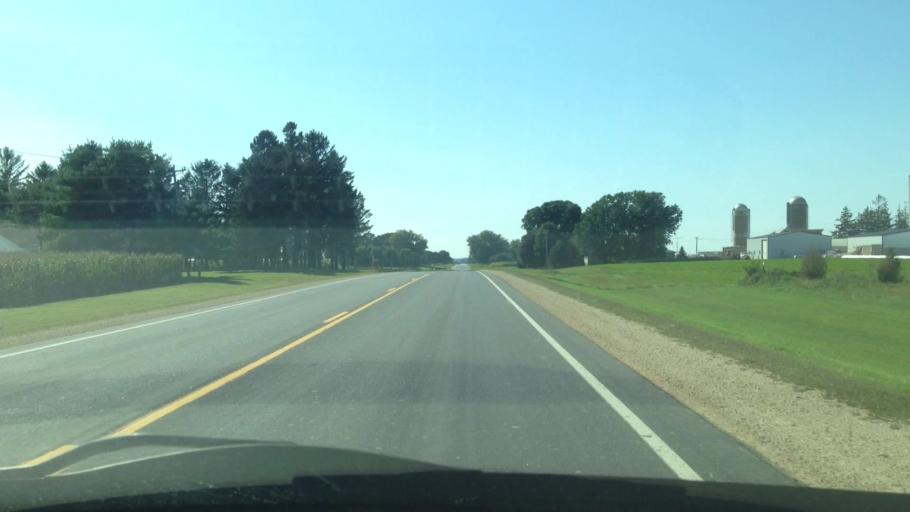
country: US
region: Minnesota
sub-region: Winona County
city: Lewiston
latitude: 43.9696
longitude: -91.8265
